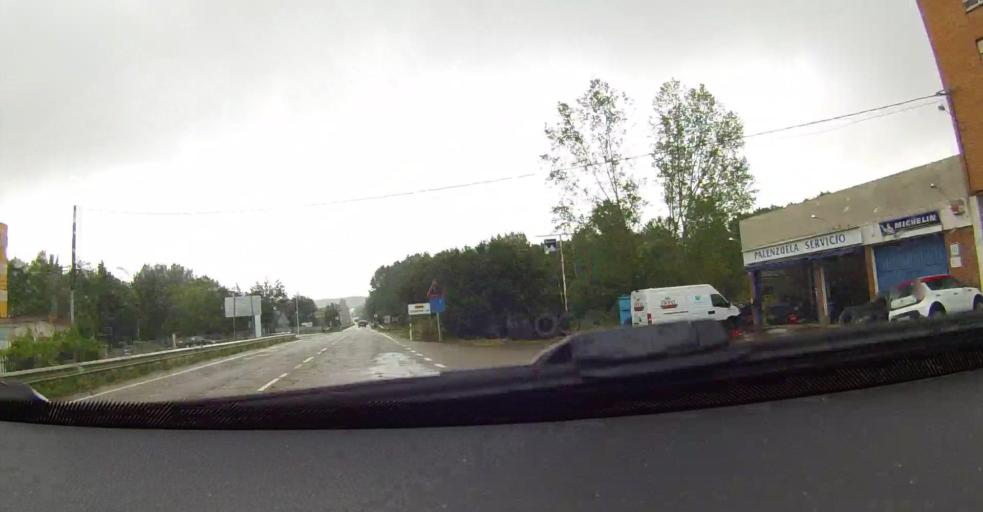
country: ES
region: Castille and Leon
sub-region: Provincia de Palencia
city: Saldana
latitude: 42.5148
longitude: -4.7389
